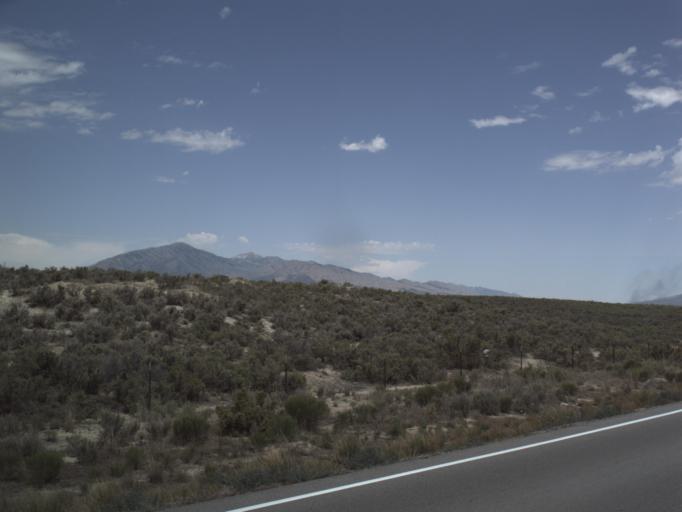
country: US
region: Utah
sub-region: Tooele County
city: Tooele
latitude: 40.2199
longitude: -112.4054
